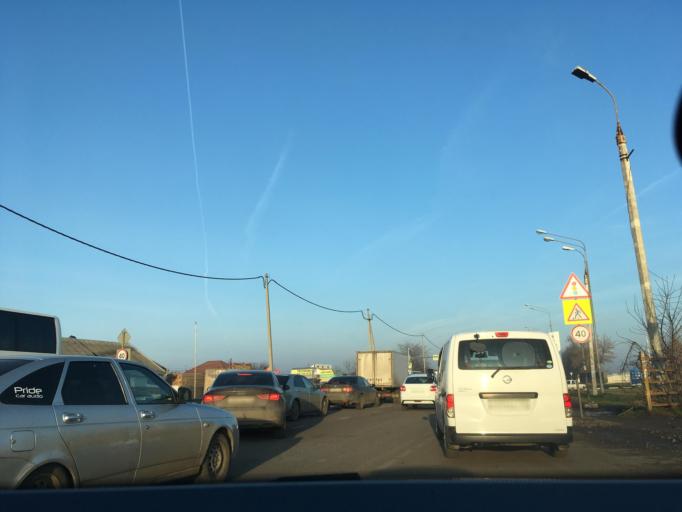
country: RU
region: Krasnodarskiy
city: Krasnodar
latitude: 45.1271
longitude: 39.0118
